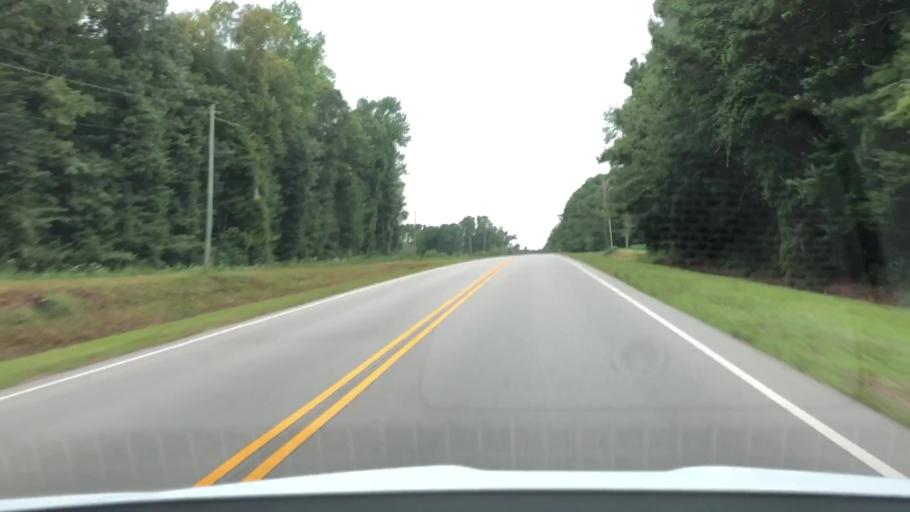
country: US
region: North Carolina
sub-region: Jones County
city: Trenton
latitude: 35.0332
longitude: -77.3200
